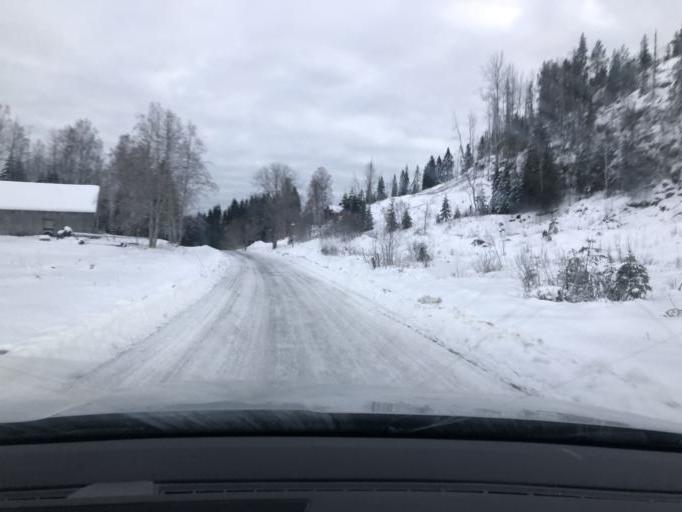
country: SE
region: Vaesternorrland
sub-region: Kramfors Kommun
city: Nordingra
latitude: 62.9069
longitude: 18.2408
